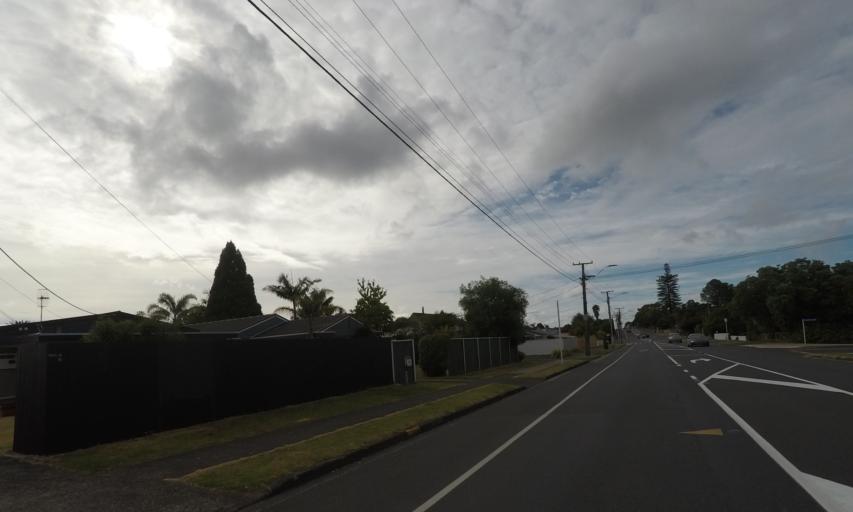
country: NZ
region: Northland
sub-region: Whangarei
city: Whangarei
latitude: -35.6872
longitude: 174.3031
